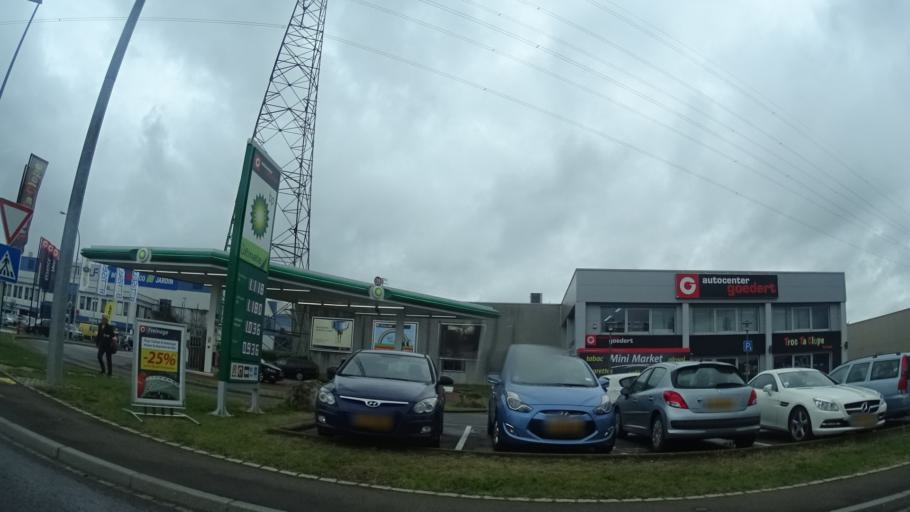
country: LU
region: Luxembourg
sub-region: Canton d'Esch-sur-Alzette
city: Schifflange
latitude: 49.5214
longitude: 6.0105
